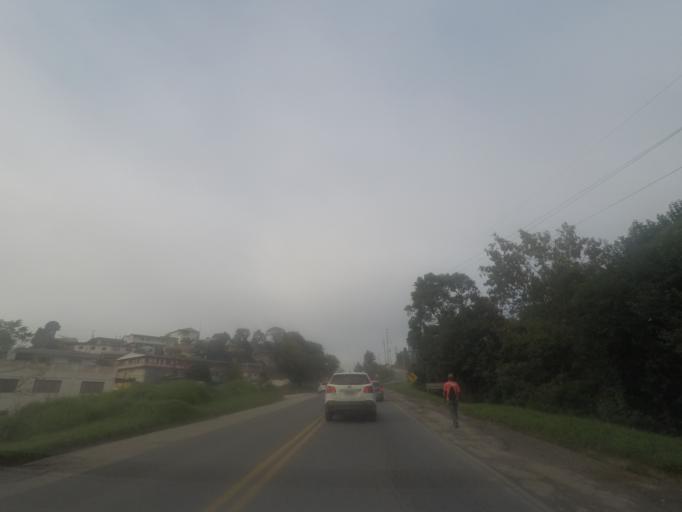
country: BR
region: Parana
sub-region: Almirante Tamandare
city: Almirante Tamandare
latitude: -25.3096
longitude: -49.3036
